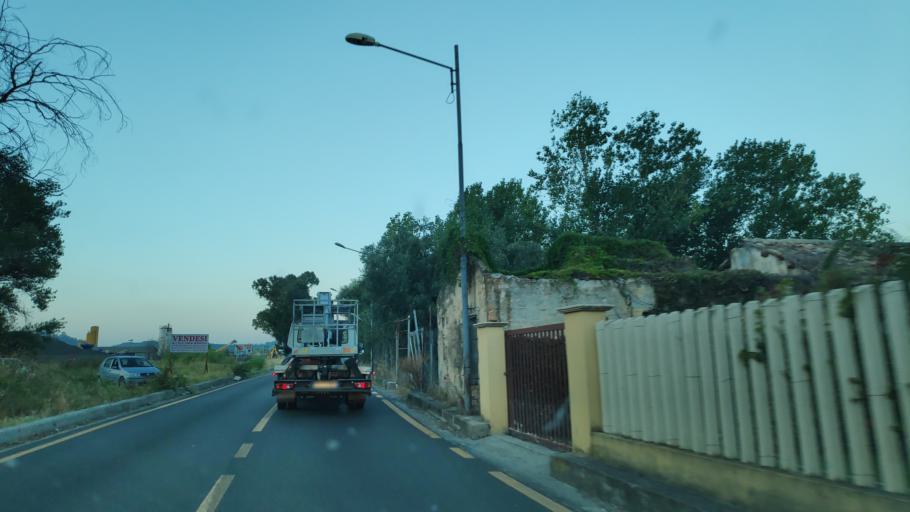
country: IT
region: Calabria
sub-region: Provincia di Reggio Calabria
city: Caulonia Marina
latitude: 38.3463
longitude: 16.4677
